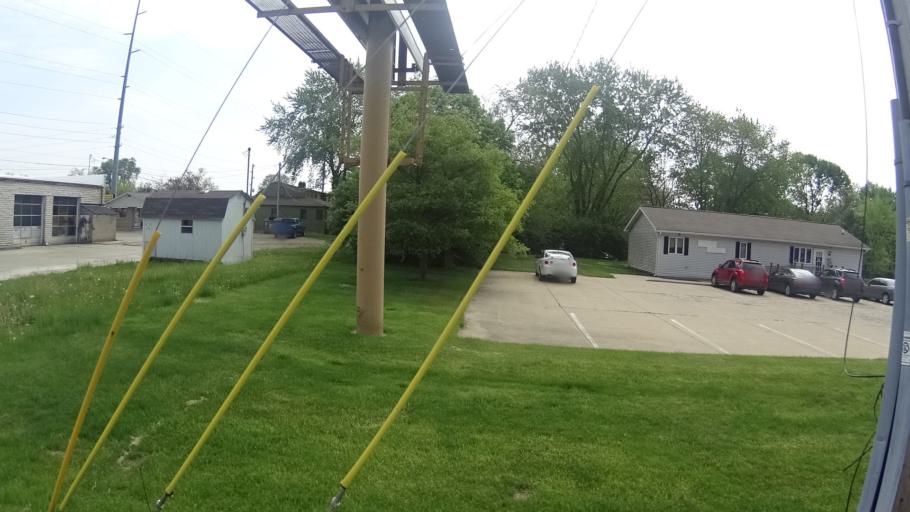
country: US
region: Indiana
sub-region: Madison County
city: Anderson
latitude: 40.1346
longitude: -85.6915
